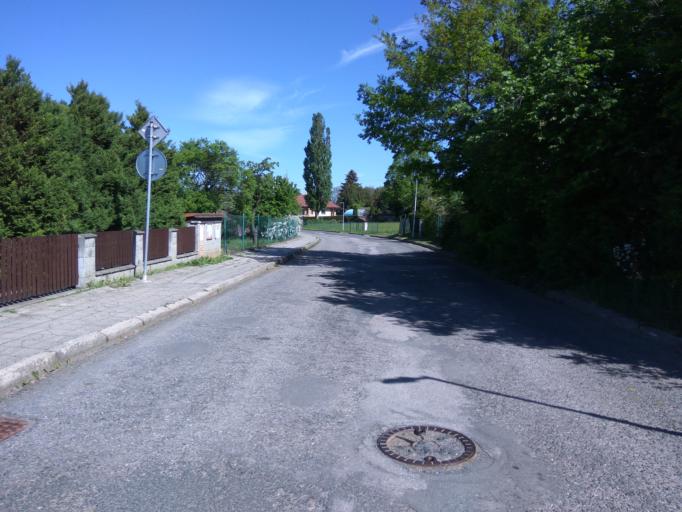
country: CZ
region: Vysocina
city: Chotebor
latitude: 49.7198
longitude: 15.6784
